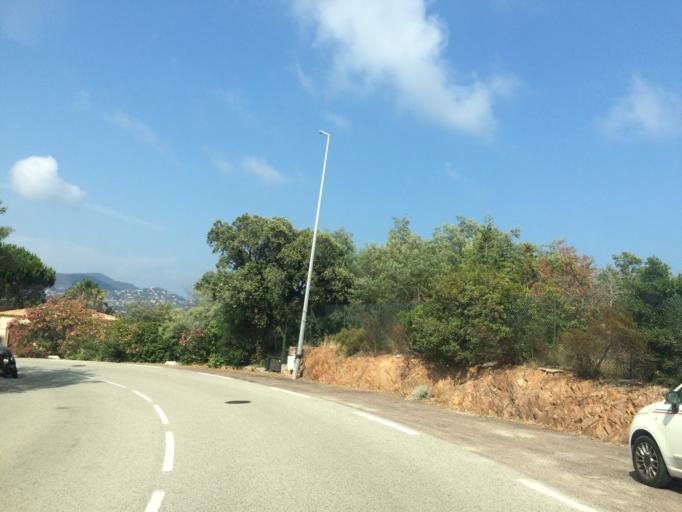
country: FR
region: Provence-Alpes-Cote d'Azur
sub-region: Departement des Alpes-Maritimes
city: Theoule-sur-Mer
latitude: 43.4632
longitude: 6.9225
